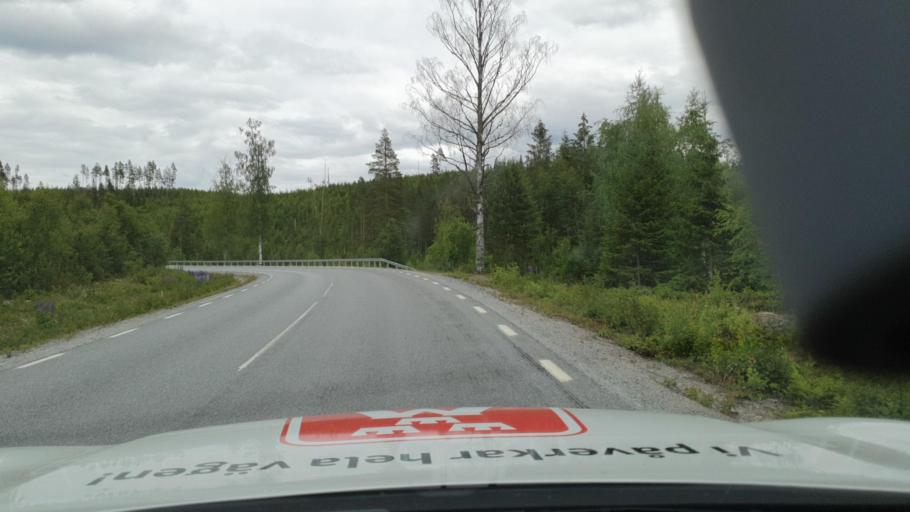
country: SE
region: Vaesterbotten
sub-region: Bjurholms Kommun
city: Bjurholm
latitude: 63.8775
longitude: 19.0120
